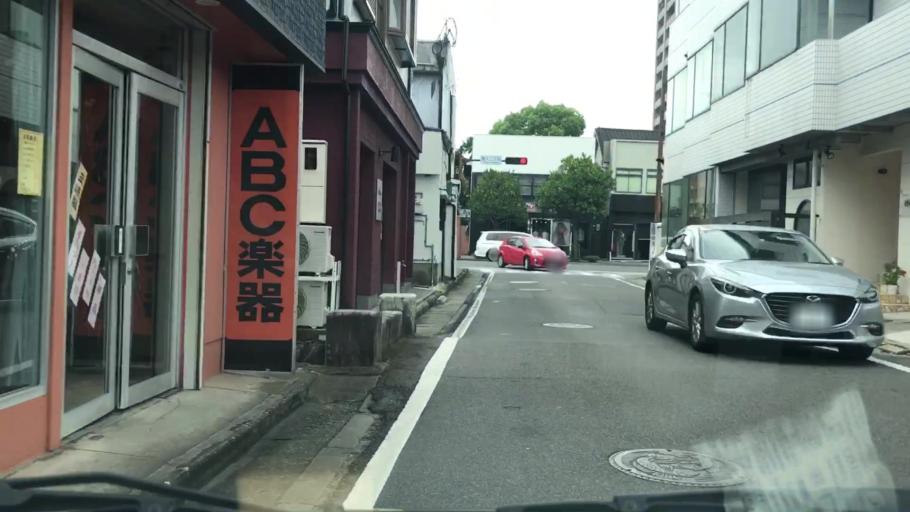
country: JP
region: Saga Prefecture
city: Saga-shi
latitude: 33.2578
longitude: 130.3002
